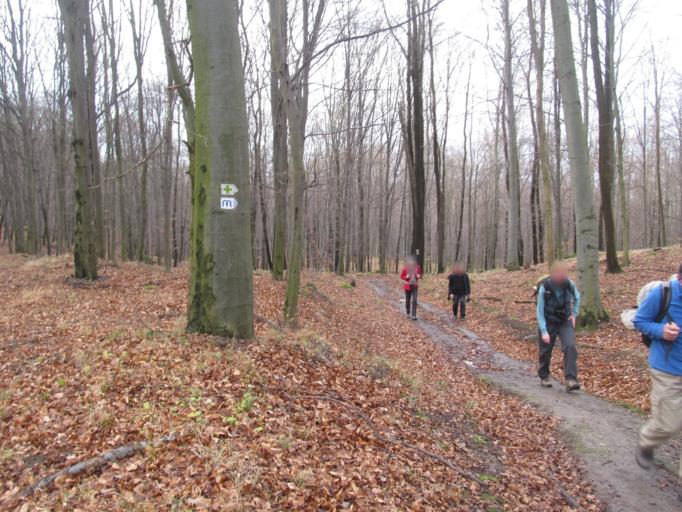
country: HU
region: Komarom-Esztergom
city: Pilismarot
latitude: 47.7383
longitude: 18.8696
